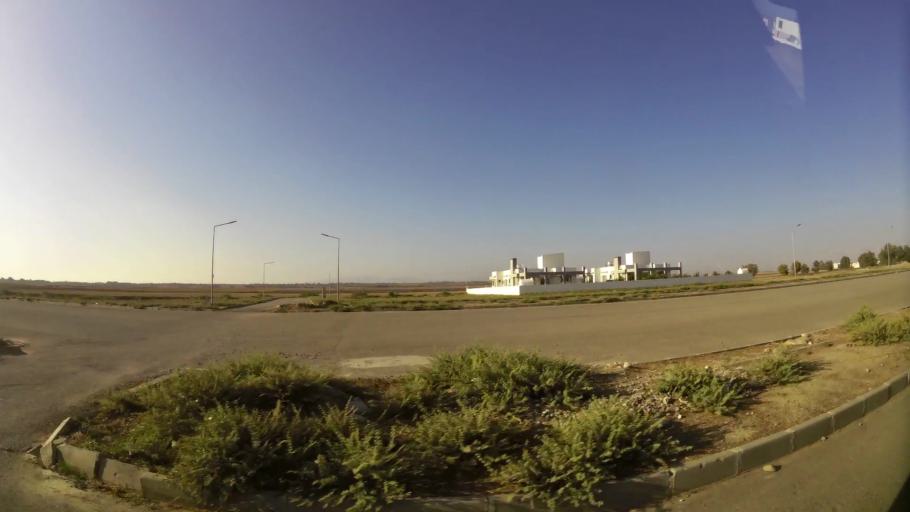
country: CY
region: Lefkosia
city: Nicosia
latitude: 35.2015
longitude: 33.3015
